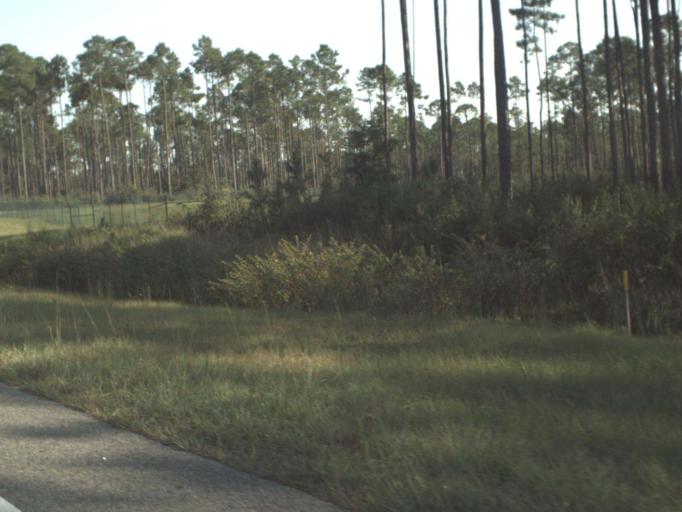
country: US
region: Florida
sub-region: Bay County
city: Laguna Beach
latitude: 30.4237
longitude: -85.8750
